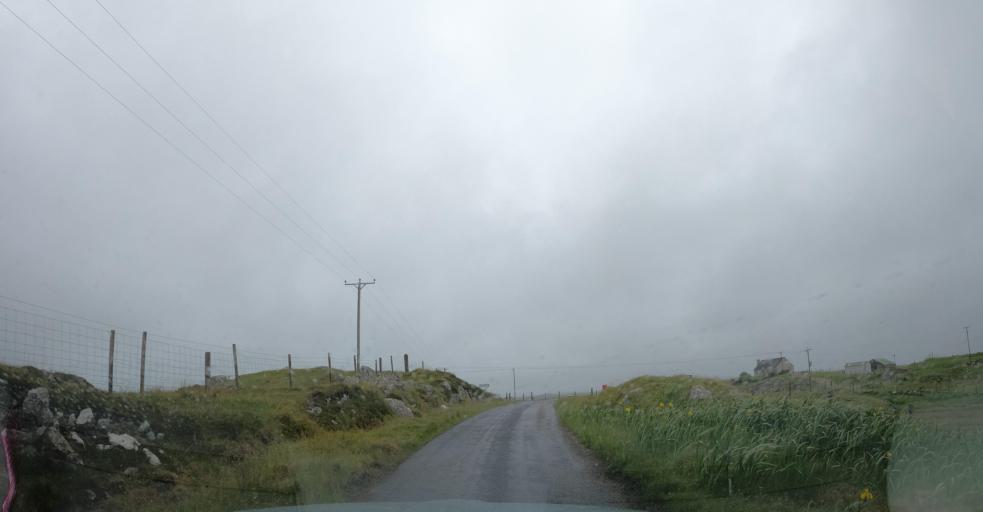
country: GB
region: Scotland
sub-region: Eilean Siar
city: Benbecula
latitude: 57.4990
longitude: -7.2486
